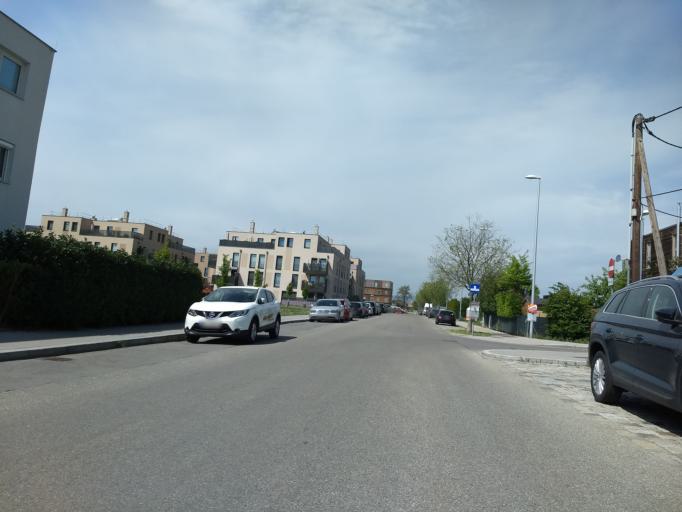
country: AT
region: Lower Austria
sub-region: Politischer Bezirk Ganserndorf
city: Aderklaa
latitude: 48.2408
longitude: 16.4984
